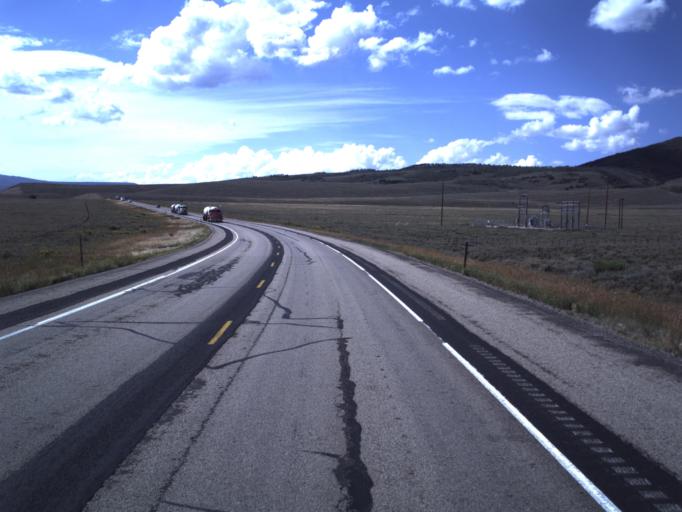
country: US
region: Utah
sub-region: Wasatch County
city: Heber
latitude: 40.2239
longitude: -111.1070
